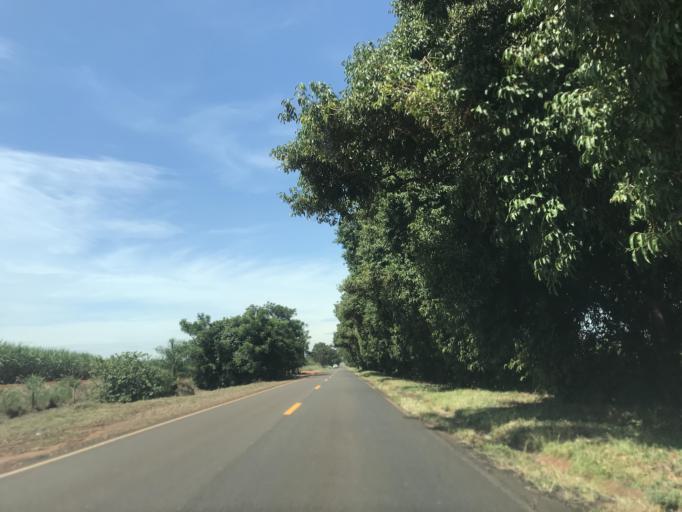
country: BR
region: Parana
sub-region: Terra Rica
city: Terra Rica
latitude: -22.8076
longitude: -52.6540
